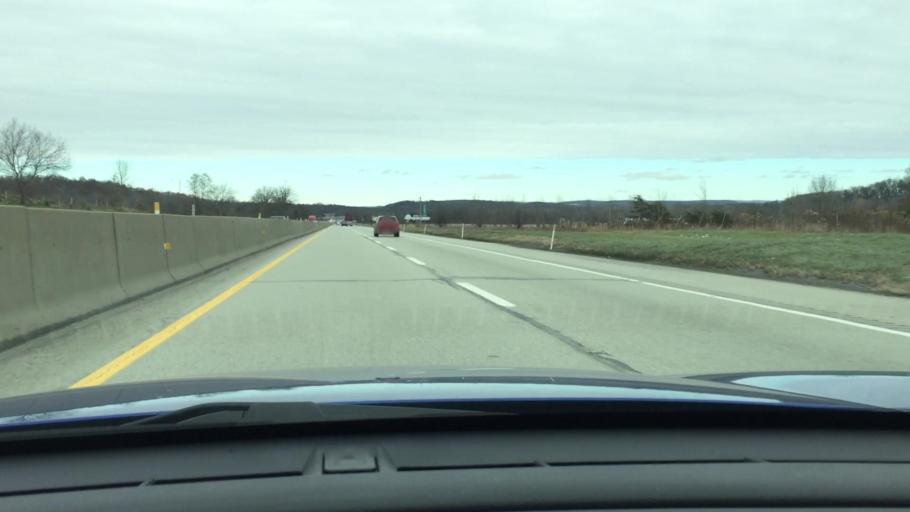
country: US
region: Pennsylvania
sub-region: Somerset County
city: Central City
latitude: 39.9889
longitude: -78.7041
